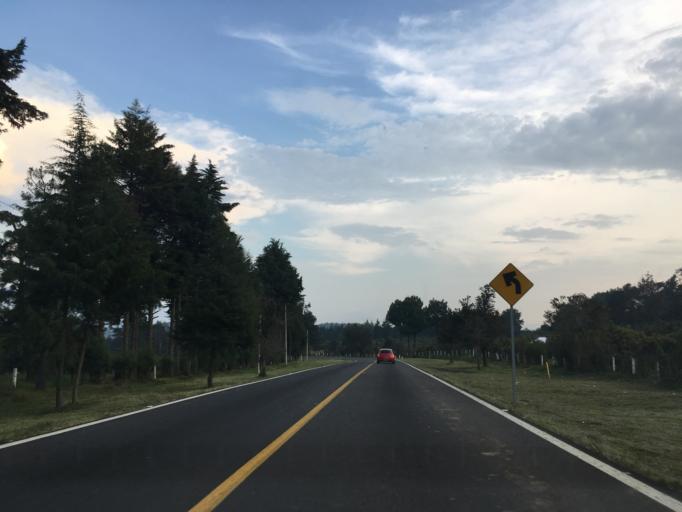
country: MX
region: Michoacan
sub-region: Patzcuaro
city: Santa Maria Huiramangaro (San Juan Tumbio)
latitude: 19.4949
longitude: -101.7496
